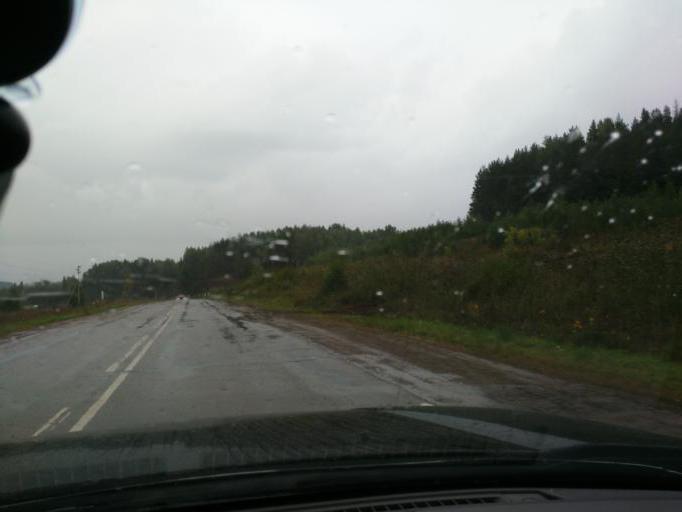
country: RU
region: Perm
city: Osa
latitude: 57.2157
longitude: 55.5915
